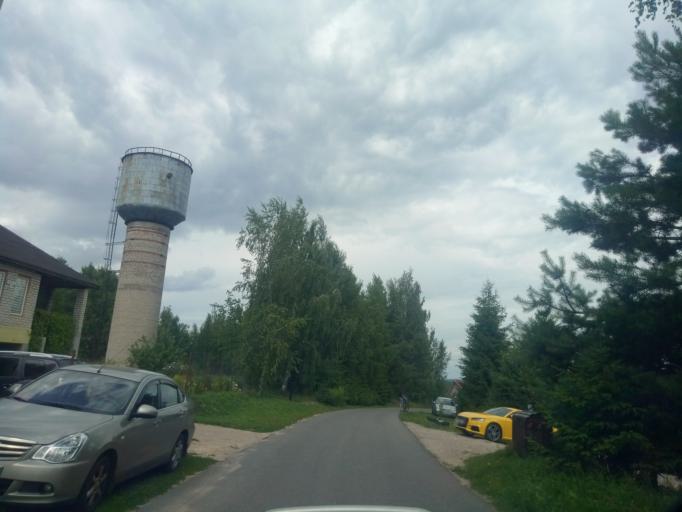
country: BY
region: Minsk
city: Zhdanovichy
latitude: 53.9363
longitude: 27.4180
